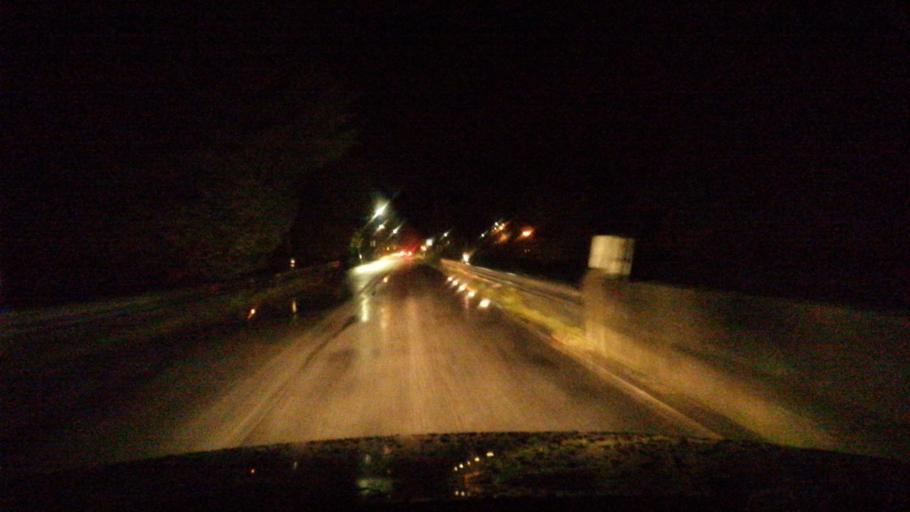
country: PT
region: Viseu
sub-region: Sernancelhe
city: Sernancelhe
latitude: 40.8912
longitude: -7.5164
